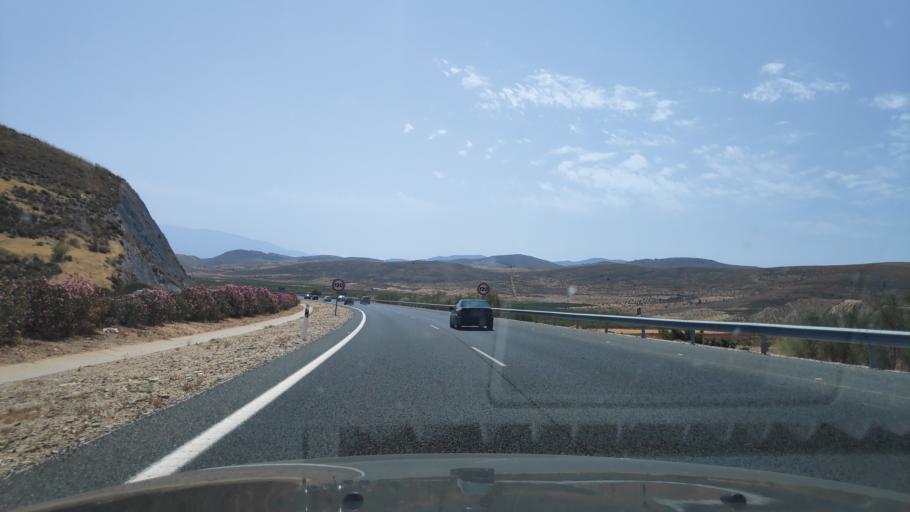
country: ES
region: Andalusia
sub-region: Provincia de Granada
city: Padul
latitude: 36.9947
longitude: -3.6287
